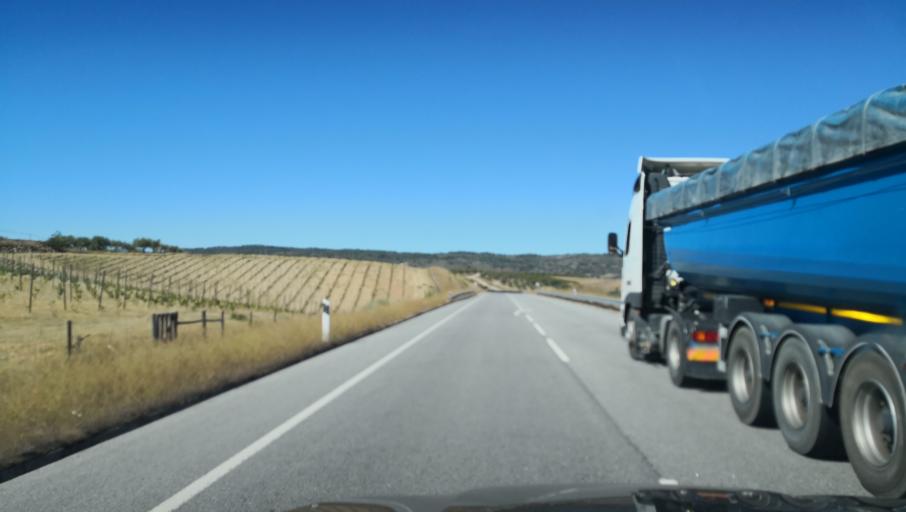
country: PT
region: Vila Real
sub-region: Valpacos
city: Valpacos
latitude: 41.5472
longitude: -7.2584
